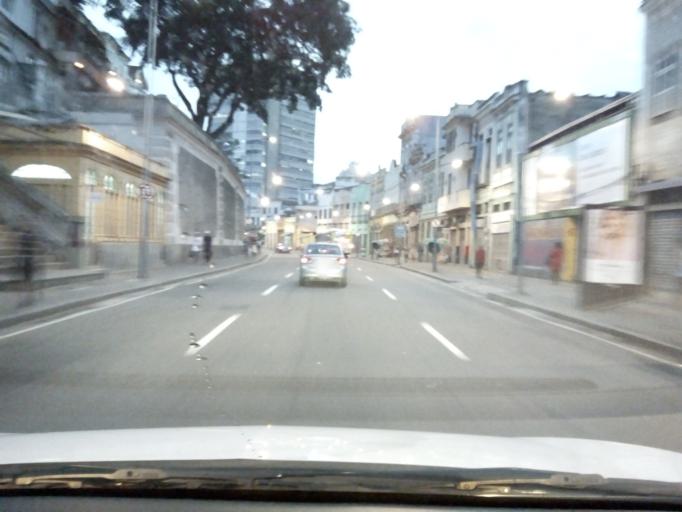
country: BR
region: Rio de Janeiro
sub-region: Rio De Janeiro
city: Rio de Janeiro
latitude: -22.8978
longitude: -43.1875
